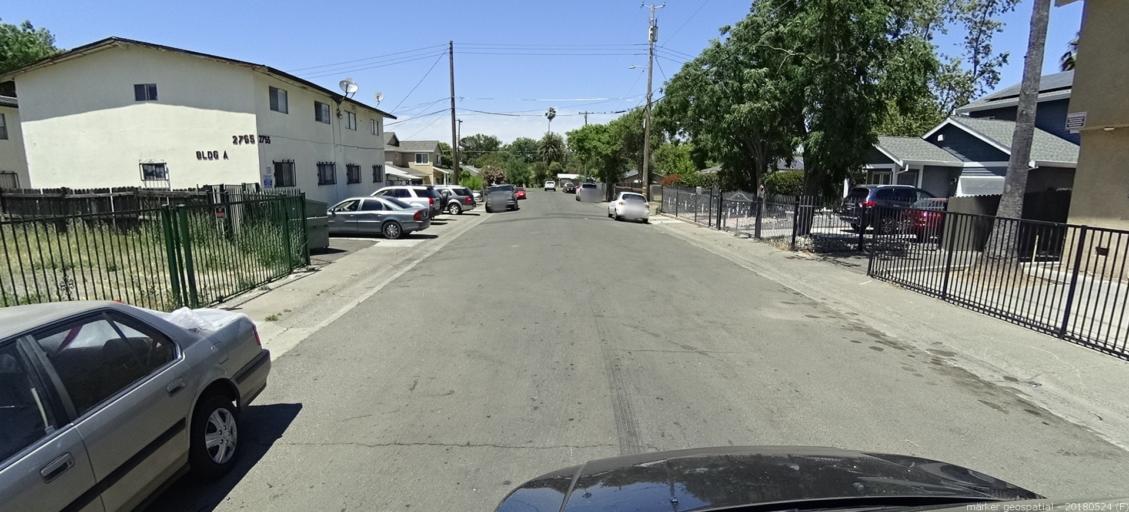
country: US
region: California
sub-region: Sacramento County
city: Sacramento
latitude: 38.6175
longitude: -121.4500
